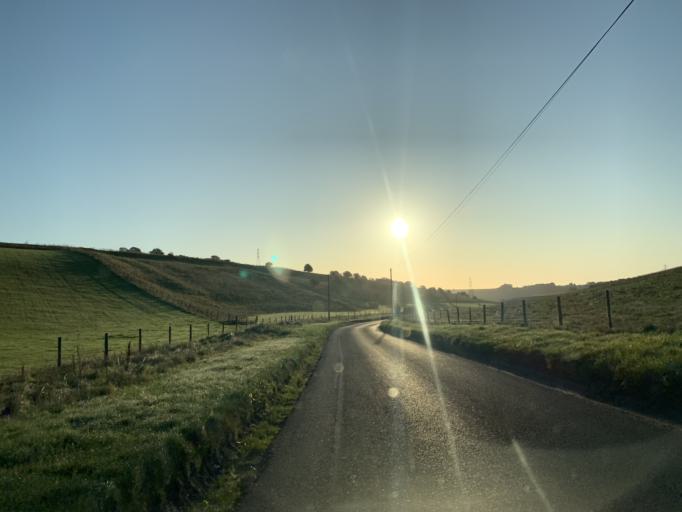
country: GB
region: England
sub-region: Wiltshire
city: Woodford
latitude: 51.1270
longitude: -1.8465
